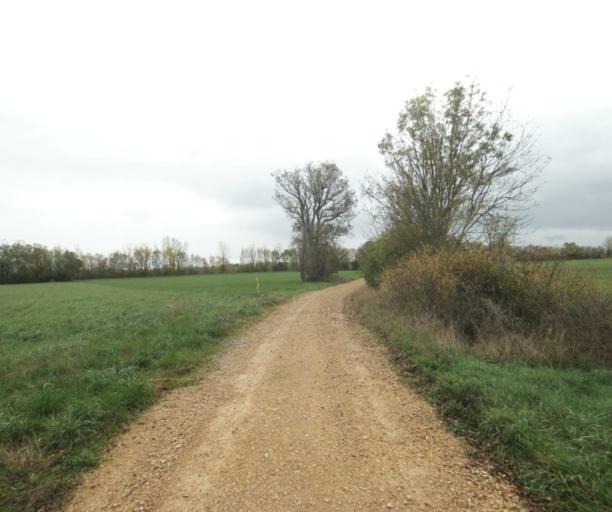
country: FR
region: Rhone-Alpes
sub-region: Departement de l'Ain
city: Pont-de-Vaux
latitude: 46.4571
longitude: 4.9028
